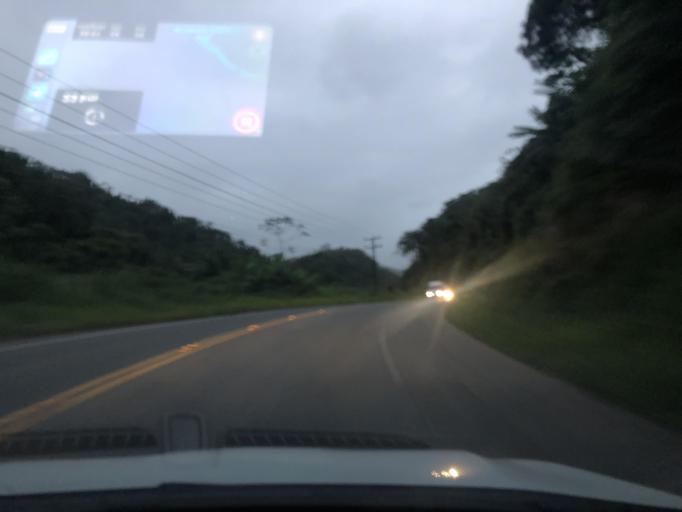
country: BR
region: Santa Catarina
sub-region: Pomerode
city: Pomerode
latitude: -26.6557
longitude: -49.0281
